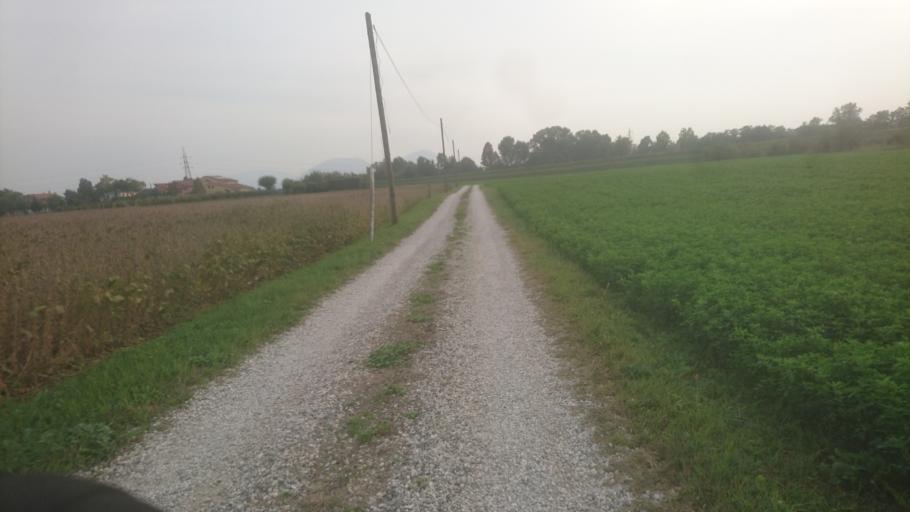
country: IT
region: Veneto
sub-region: Provincia di Vicenza
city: Montegalda
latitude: 45.4379
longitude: 11.6831
